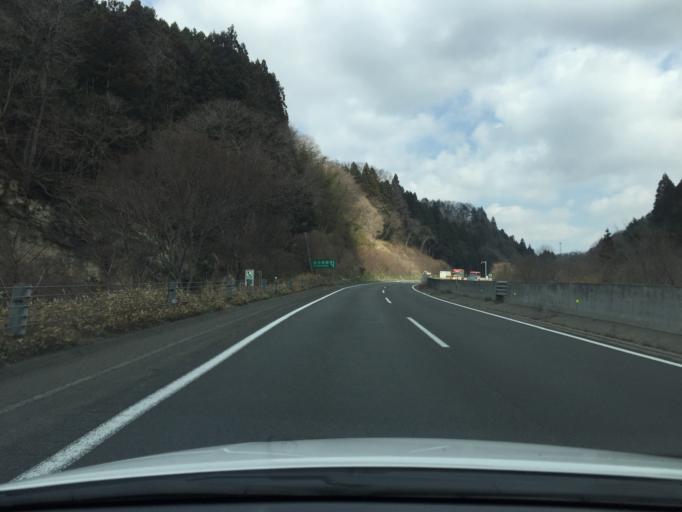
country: JP
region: Miyagi
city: Sendai
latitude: 38.2421
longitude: 140.8177
